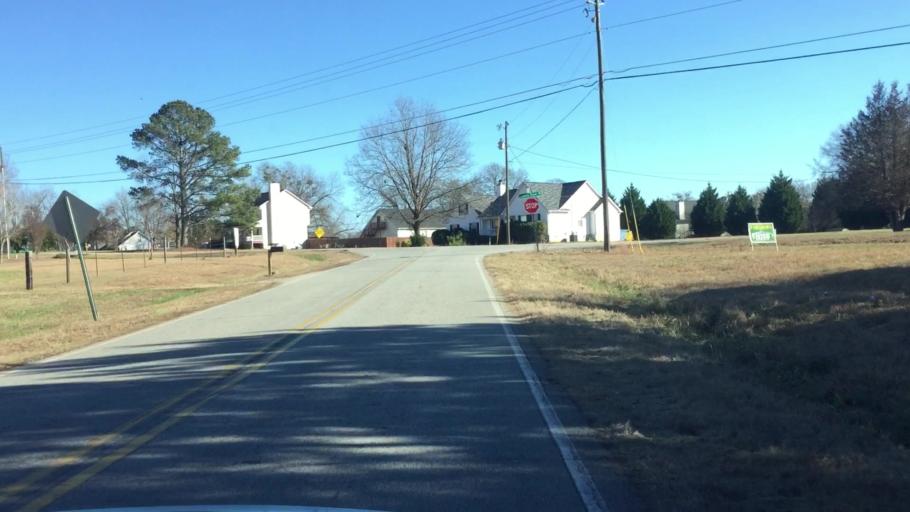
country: US
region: Georgia
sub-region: Newton County
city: Oakwood
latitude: 33.4674
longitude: -84.0109
